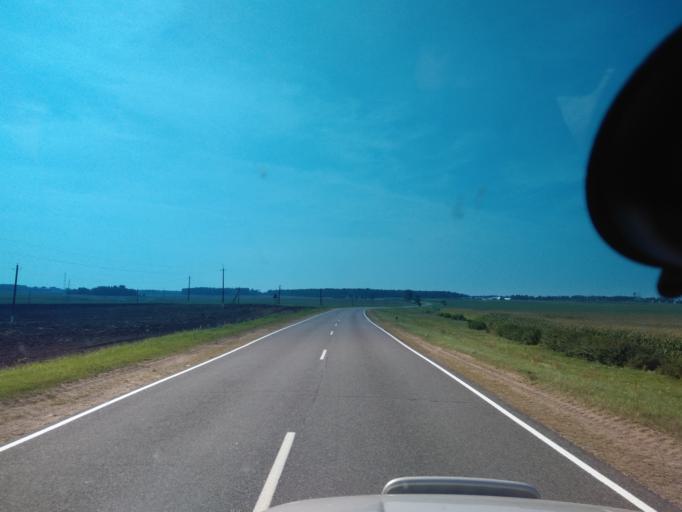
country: BY
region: Minsk
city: Uzda
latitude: 53.3689
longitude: 27.2320
